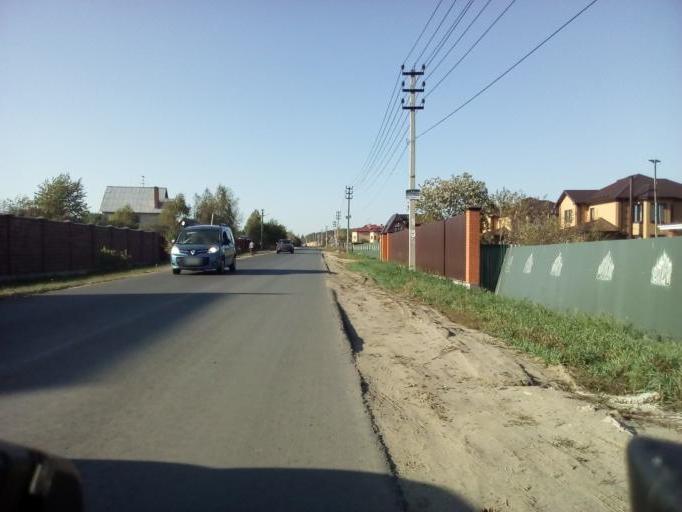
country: RU
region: Moskovskaya
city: Malyshevo
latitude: 55.5565
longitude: 38.3116
